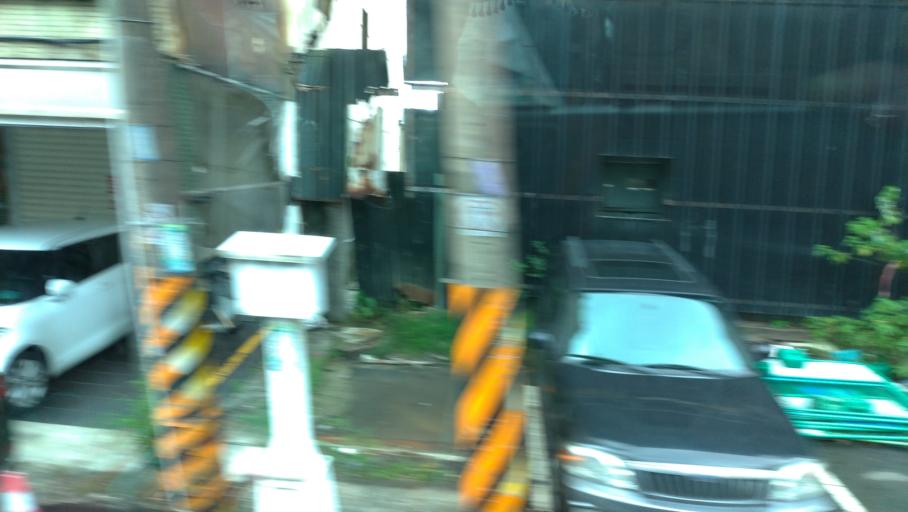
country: TW
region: Taiwan
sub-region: Keelung
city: Keelung
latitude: 25.1466
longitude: 121.7614
